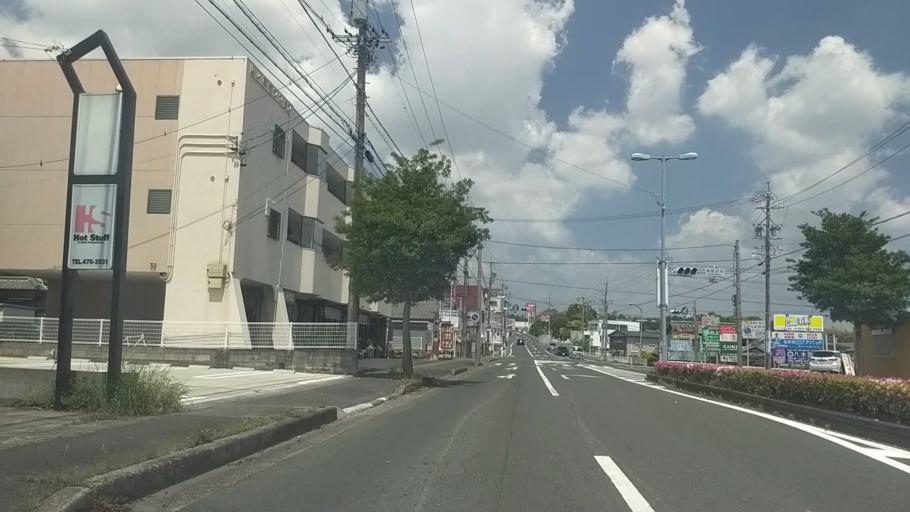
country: JP
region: Shizuoka
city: Hamamatsu
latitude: 34.7500
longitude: 137.7368
